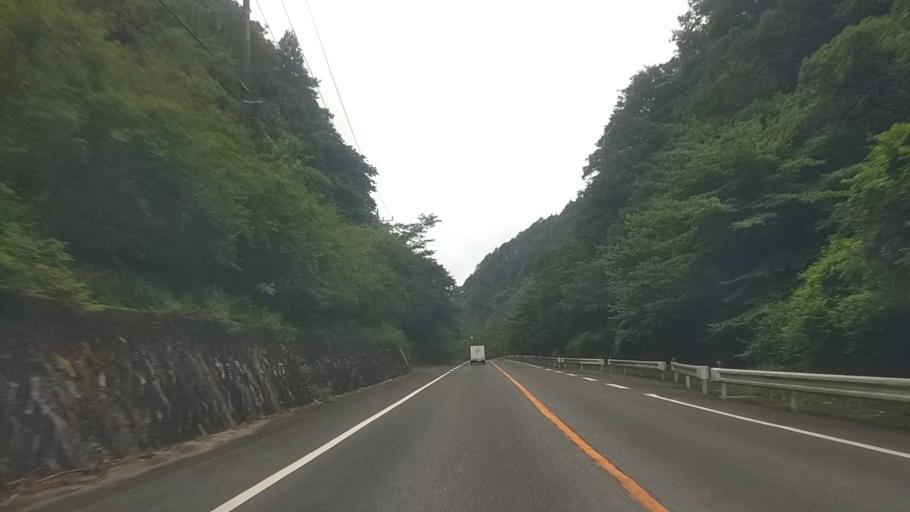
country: JP
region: Chiba
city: Kawaguchi
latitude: 35.1685
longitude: 140.0600
